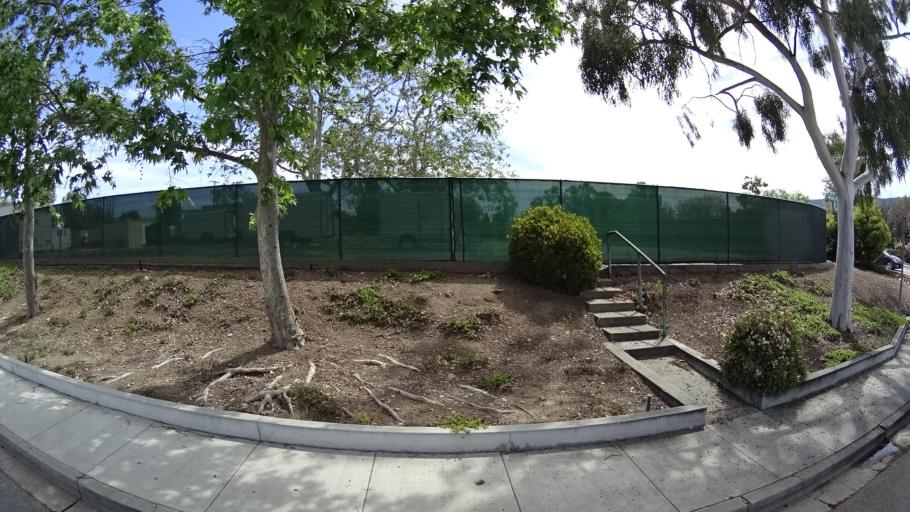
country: US
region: California
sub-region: Ventura County
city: Casa Conejo
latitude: 34.1872
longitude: -118.9268
